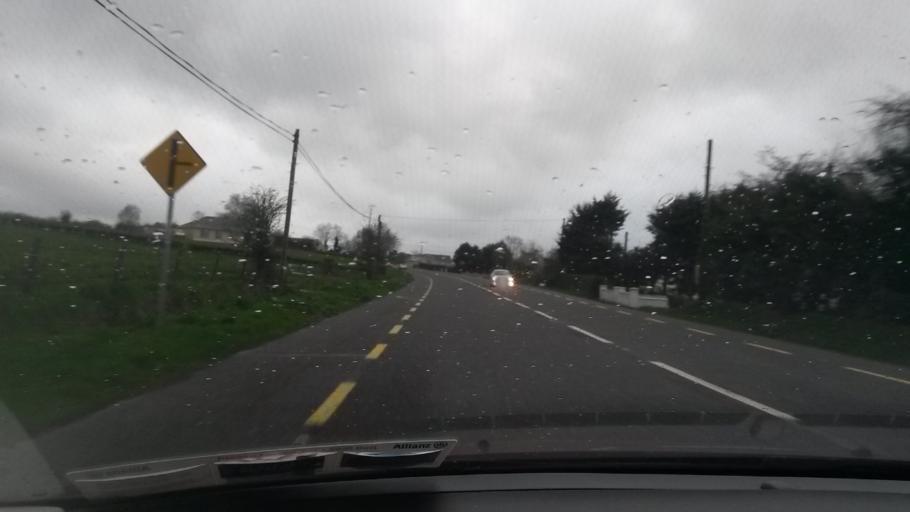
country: IE
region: Munster
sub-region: County Limerick
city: Abbeyfeale
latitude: 52.3658
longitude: -9.3232
